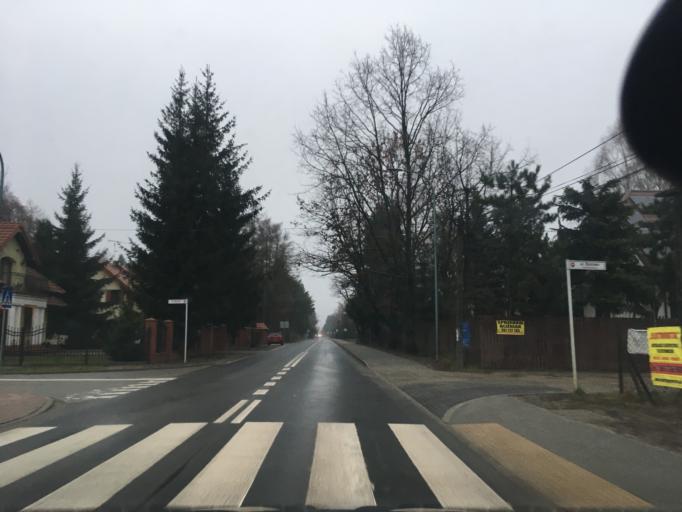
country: PL
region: Masovian Voivodeship
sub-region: Powiat piaseczynski
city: Piaseczno
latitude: 52.0577
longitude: 20.9819
